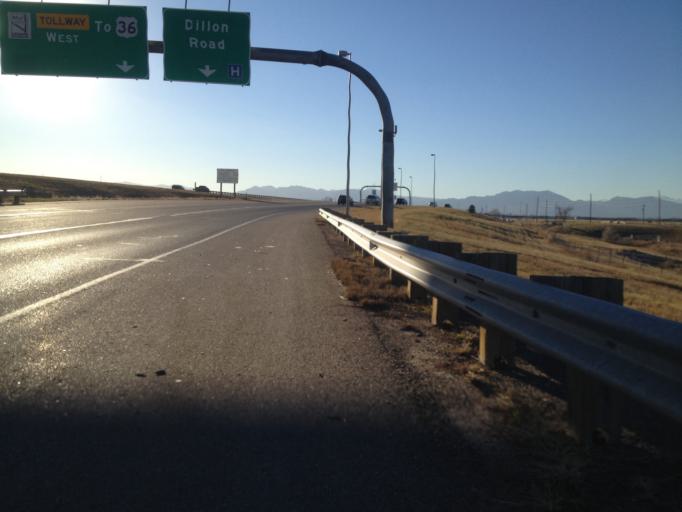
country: US
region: Colorado
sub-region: Boulder County
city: Lafayette
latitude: 39.9594
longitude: -105.0924
